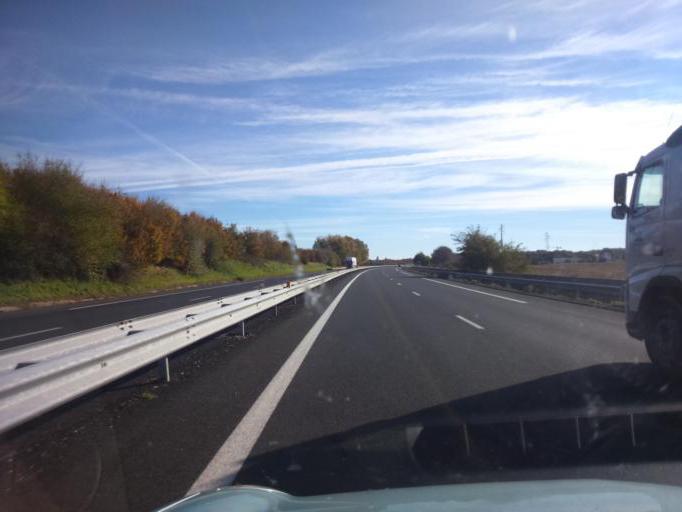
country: FR
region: Poitou-Charentes
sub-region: Departement de la Charente-Maritime
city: Tonnay-Charente
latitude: 45.9572
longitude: -0.9166
